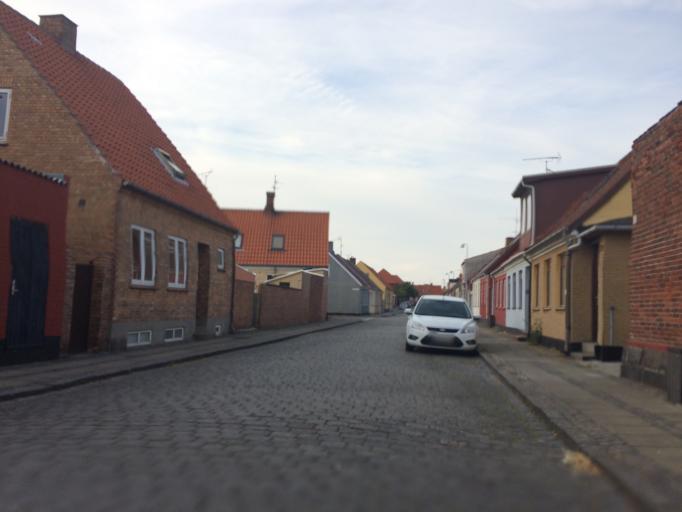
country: DK
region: Capital Region
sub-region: Bornholm Kommune
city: Ronne
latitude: 55.0980
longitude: 14.7061
